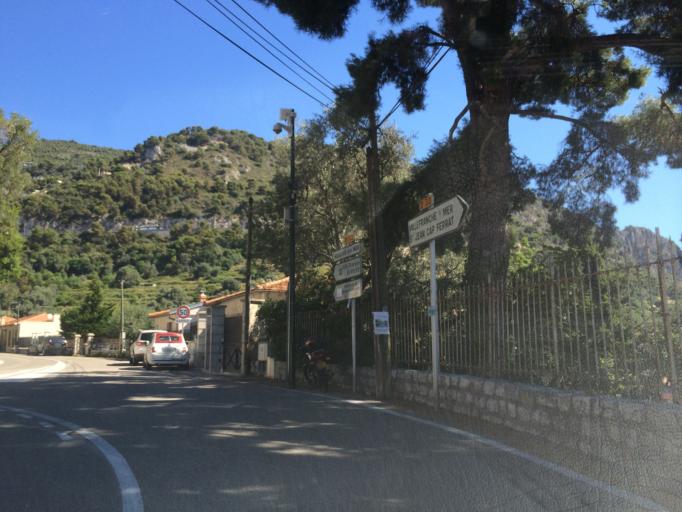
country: FR
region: Provence-Alpes-Cote d'Azur
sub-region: Departement des Alpes-Maritimes
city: Beaulieu-sur-Mer
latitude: 43.7087
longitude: 7.3234
